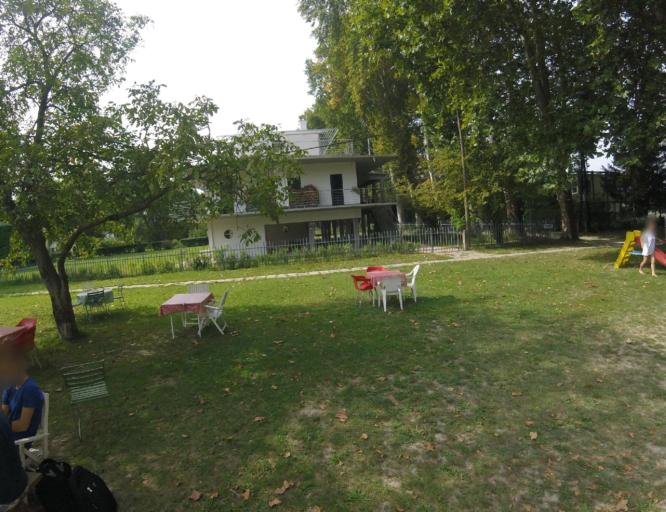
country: HU
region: Pest
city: Budakalasz
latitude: 47.6168
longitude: 19.0862
